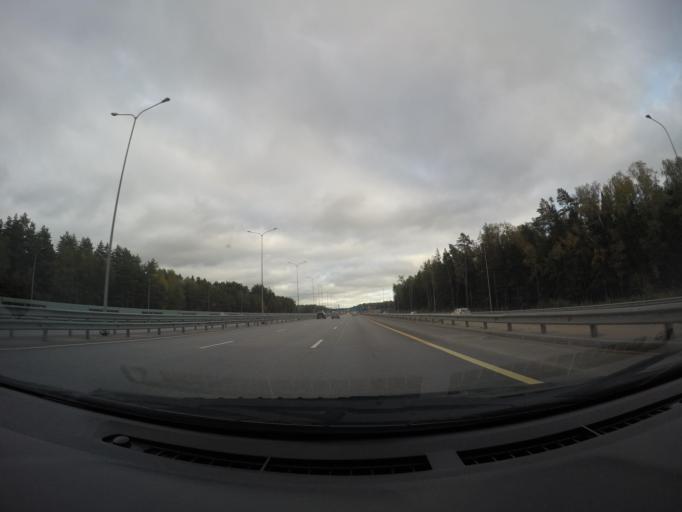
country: RU
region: Moskovskaya
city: Golitsyno
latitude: 55.5990
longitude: 36.9712
